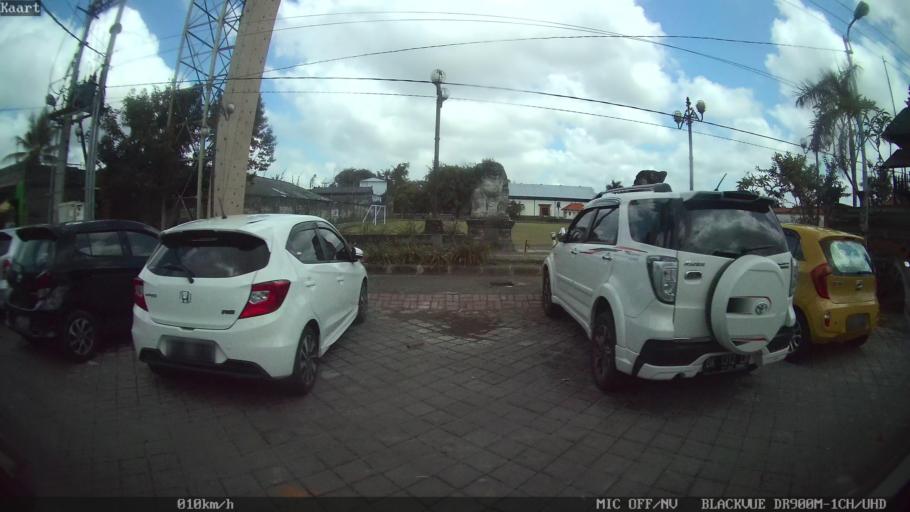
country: ID
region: Bali
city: Banjar Sedang
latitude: -8.5681
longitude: 115.2943
